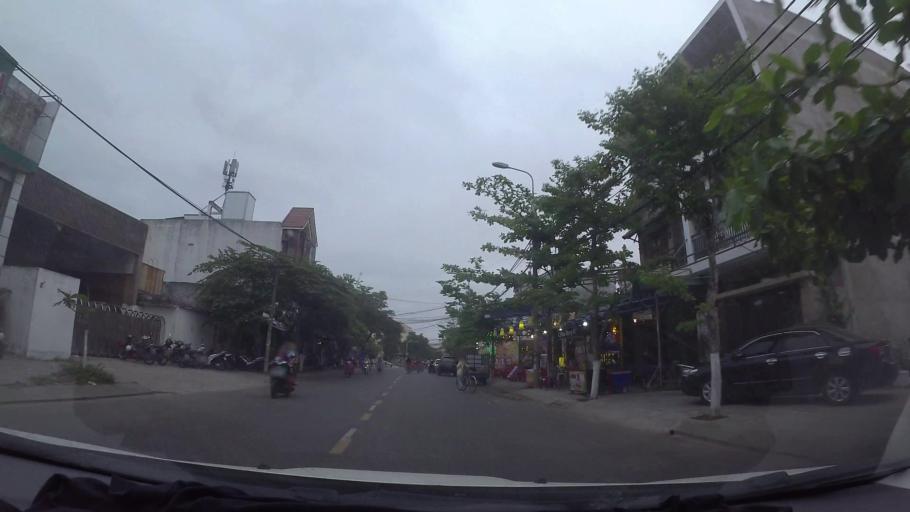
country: VN
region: Da Nang
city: Lien Chieu
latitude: 16.0710
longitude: 108.1551
